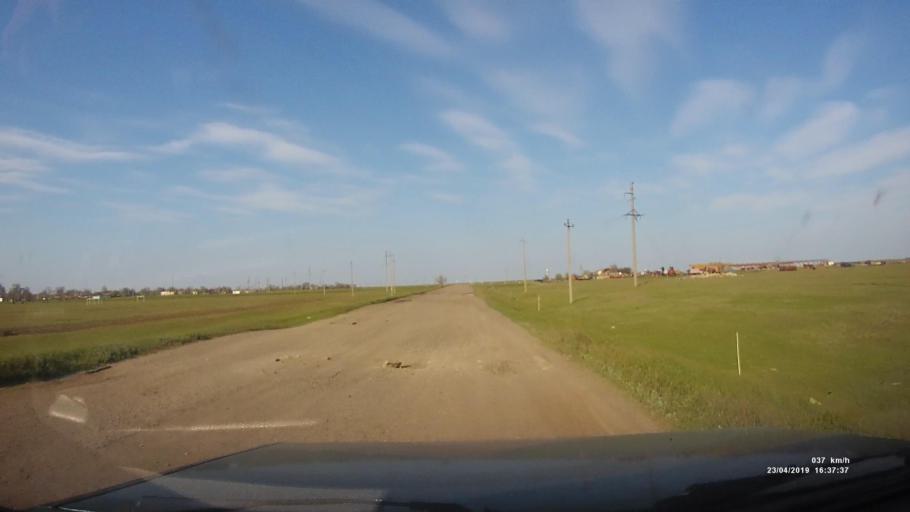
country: RU
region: Kalmykiya
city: Priyutnoye
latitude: 46.3329
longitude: 43.1465
